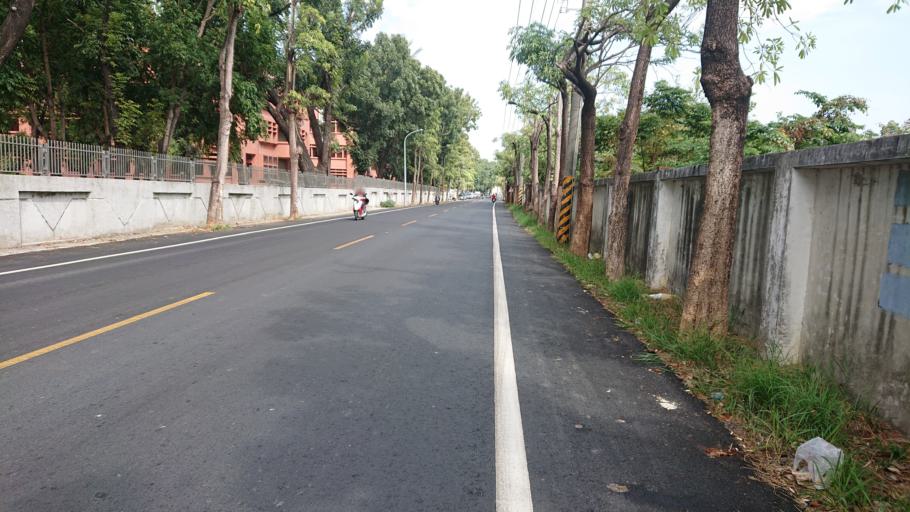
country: TW
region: Taiwan
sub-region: Tainan
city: Tainan
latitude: 23.0207
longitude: 120.2552
